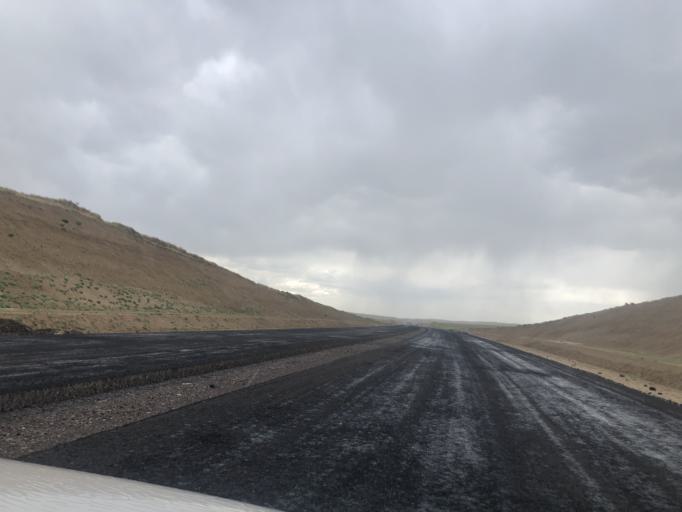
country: KG
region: Chuy
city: Bystrovka
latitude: 43.3206
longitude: 75.8862
